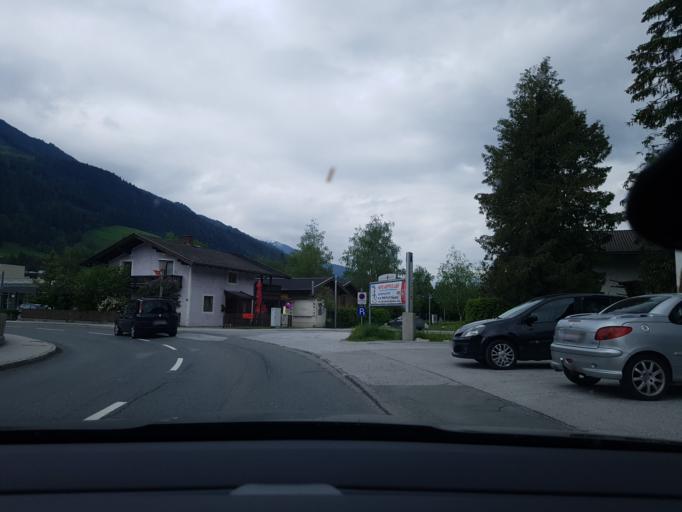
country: AT
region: Salzburg
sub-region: Politischer Bezirk Zell am See
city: Mittersill
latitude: 47.2804
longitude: 12.4800
